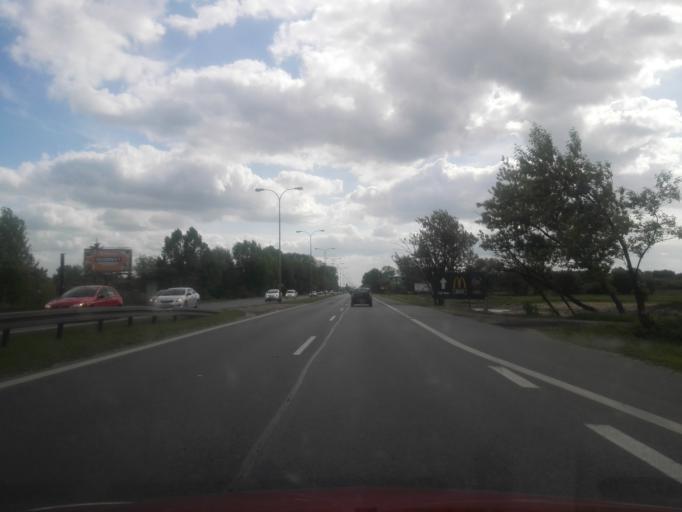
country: PL
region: Masovian Voivodeship
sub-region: Powiat wolominski
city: Zabki
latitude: 52.2994
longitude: 21.0856
